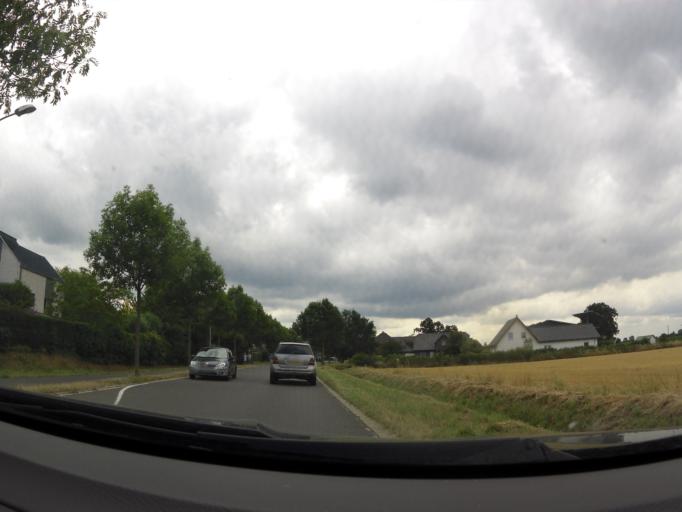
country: DE
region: North Rhine-Westphalia
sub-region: Regierungsbezirk Dusseldorf
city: Kevelaer
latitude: 51.5755
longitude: 6.2375
